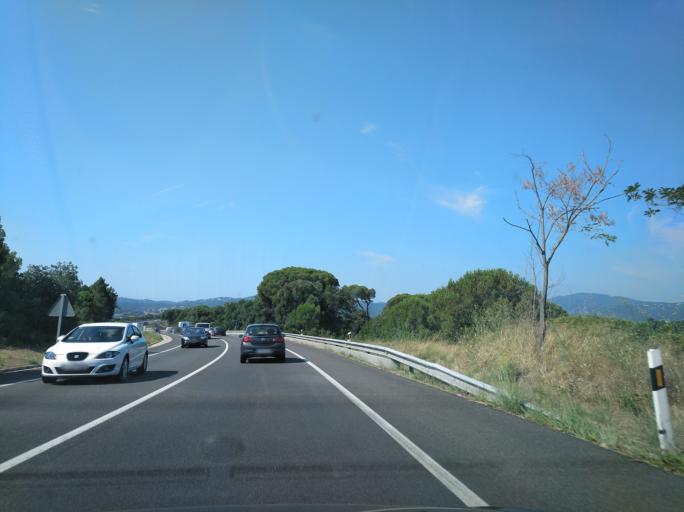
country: ES
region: Catalonia
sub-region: Provincia de Barcelona
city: Tordera
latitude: 41.7230
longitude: 2.7359
